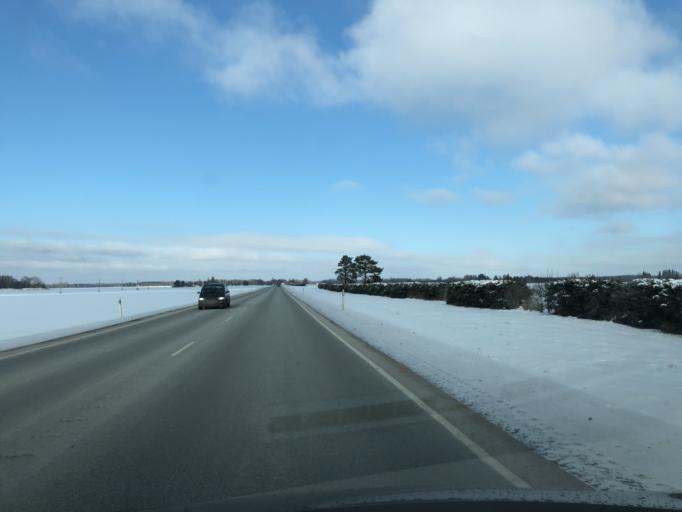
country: EE
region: Jaervamaa
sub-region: Paide linn
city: Paide
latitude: 58.7745
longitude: 25.7621
